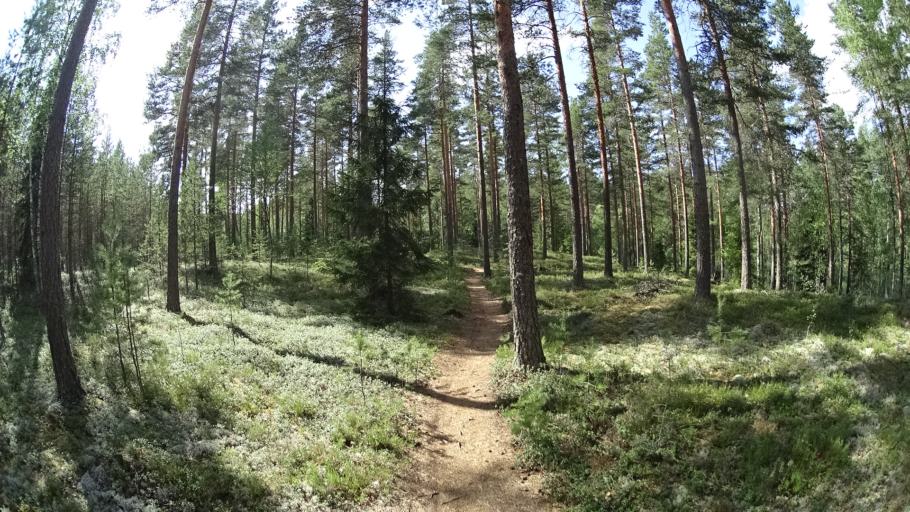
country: FI
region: Uusimaa
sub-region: Helsinki
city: Kaerkoelae
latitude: 60.7343
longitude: 24.0623
